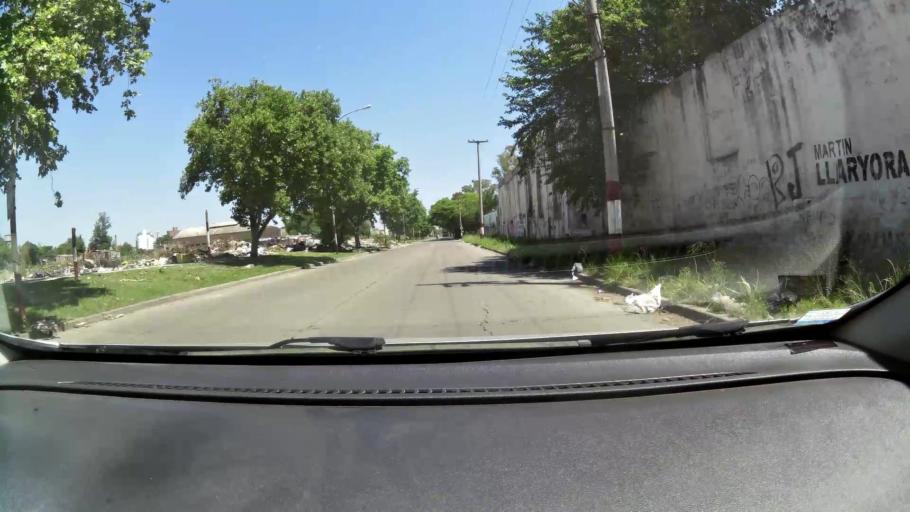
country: AR
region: Cordoba
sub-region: Departamento de Capital
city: Cordoba
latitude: -31.3899
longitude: -64.1925
